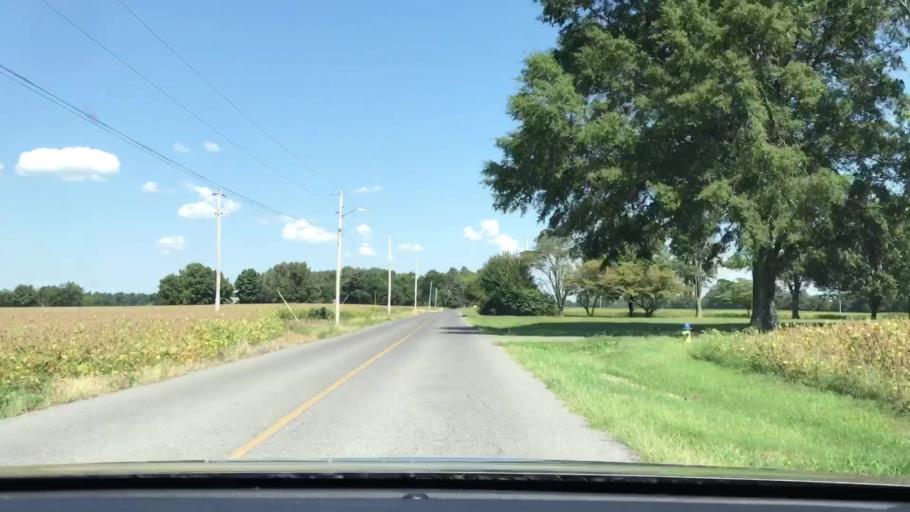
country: US
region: Kentucky
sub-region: Fulton County
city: Fulton
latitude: 36.5187
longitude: -88.9014
